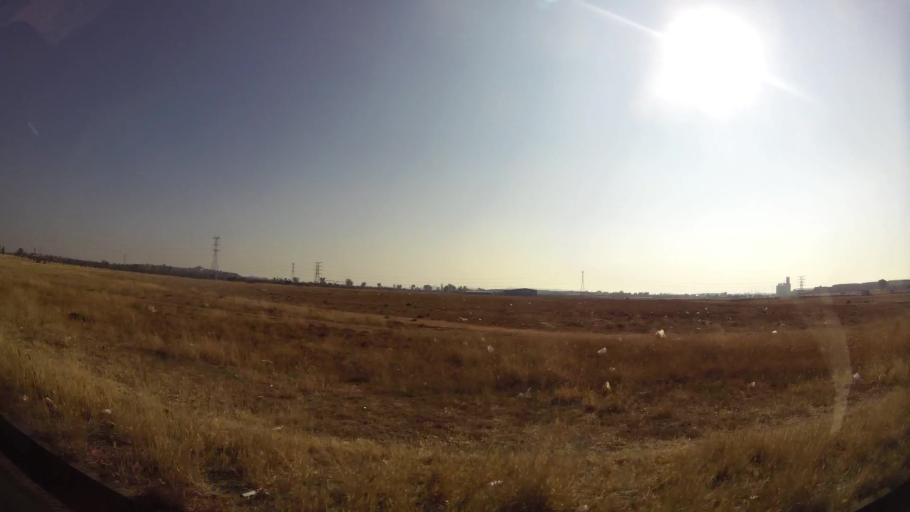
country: ZA
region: Orange Free State
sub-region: Mangaung Metropolitan Municipality
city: Bloemfontein
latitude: -29.1718
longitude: 26.2148
